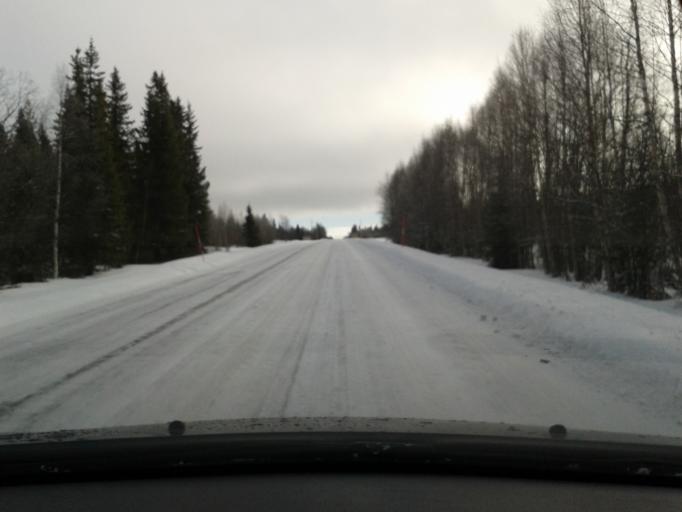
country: SE
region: Vaesterbotten
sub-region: Vilhelmina Kommun
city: Sjoberg
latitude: 64.7911
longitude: 16.0933
